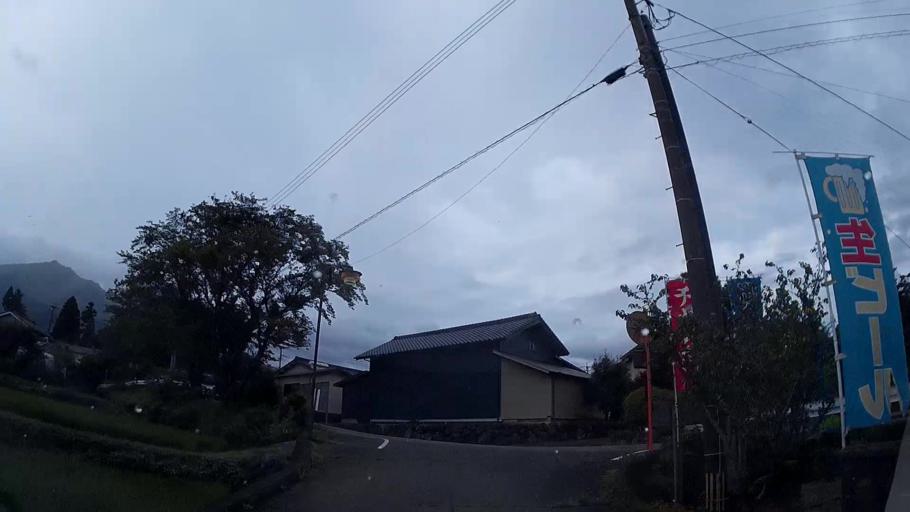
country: JP
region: Kumamoto
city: Aso
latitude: 32.8348
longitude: 131.0411
